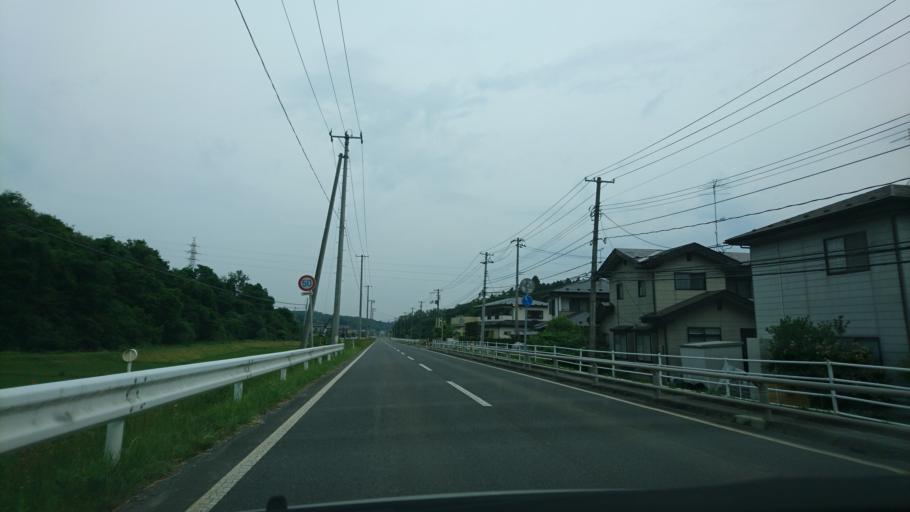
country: JP
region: Iwate
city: Ichinoseki
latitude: 38.8915
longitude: 141.1320
